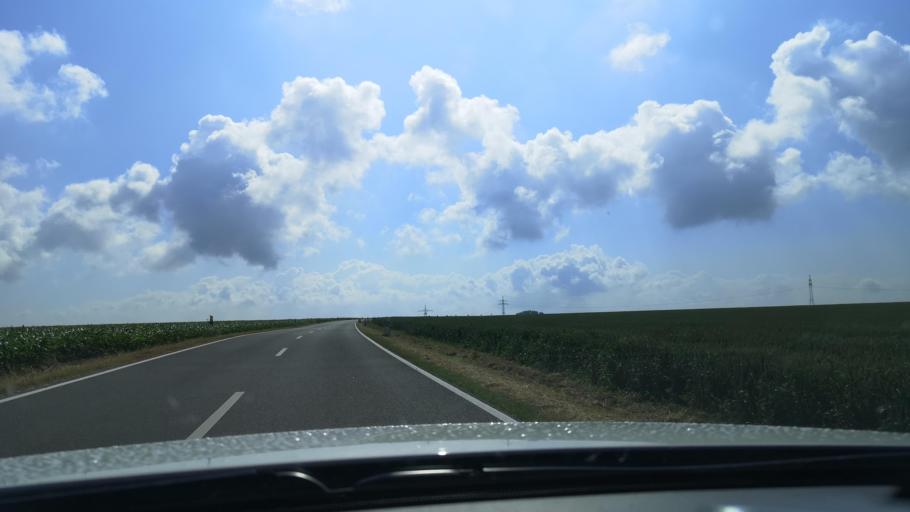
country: DE
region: Thuringia
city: Hainichen
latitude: 51.0123
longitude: 11.6060
